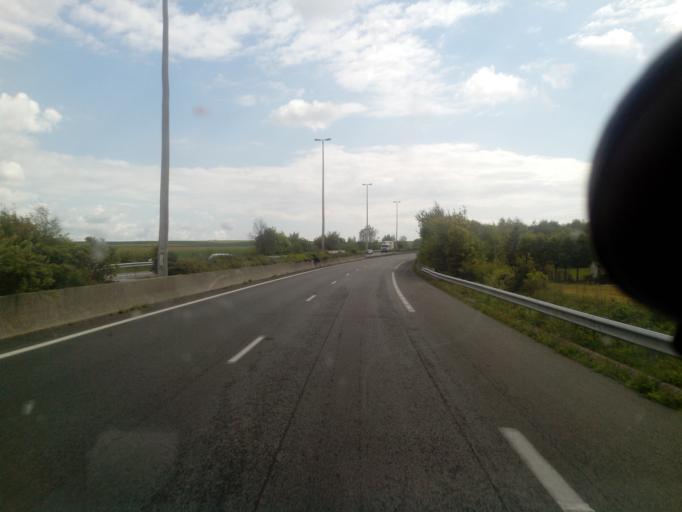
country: FR
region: Nord-Pas-de-Calais
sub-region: Departement du Pas-de-Calais
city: Ferques
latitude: 50.8716
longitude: 1.7491
